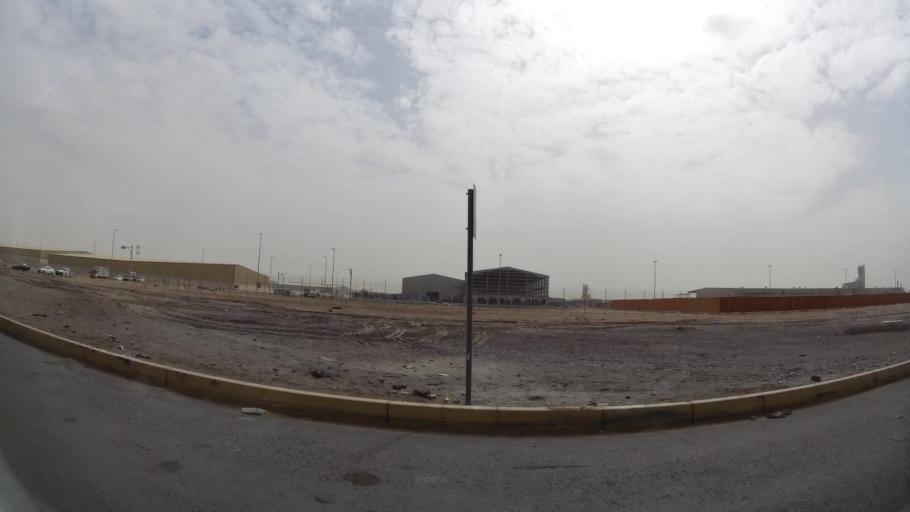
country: AE
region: Abu Dhabi
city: Abu Dhabi
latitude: 24.3372
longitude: 54.5157
